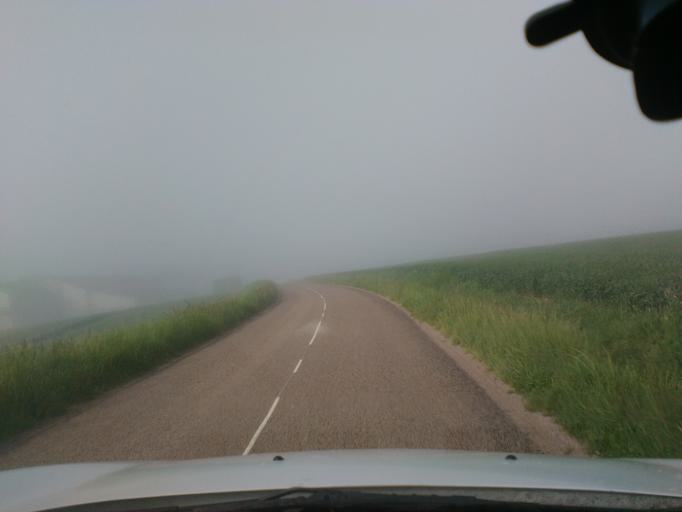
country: FR
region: Lorraine
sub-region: Departement des Vosges
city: Charmes
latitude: 48.3549
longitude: 6.2454
